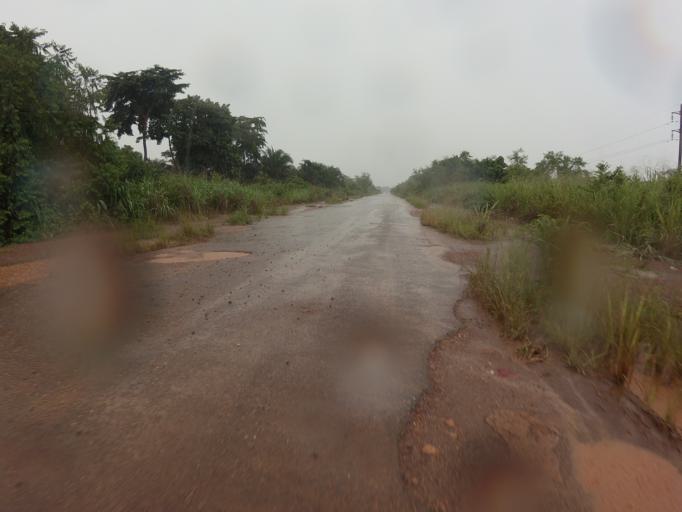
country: GH
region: Volta
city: Hohoe
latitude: 7.0658
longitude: 0.4337
